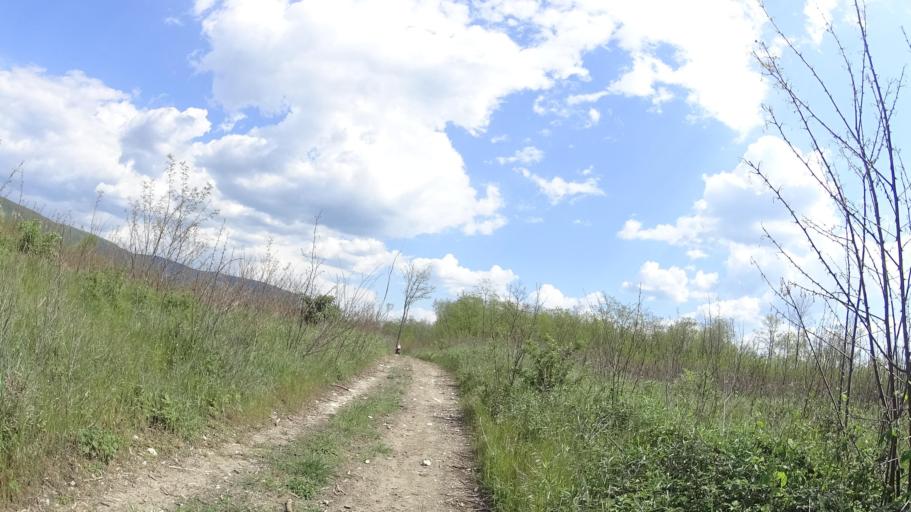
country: HU
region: Komarom-Esztergom
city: Dorog
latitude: 47.7158
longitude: 18.7646
